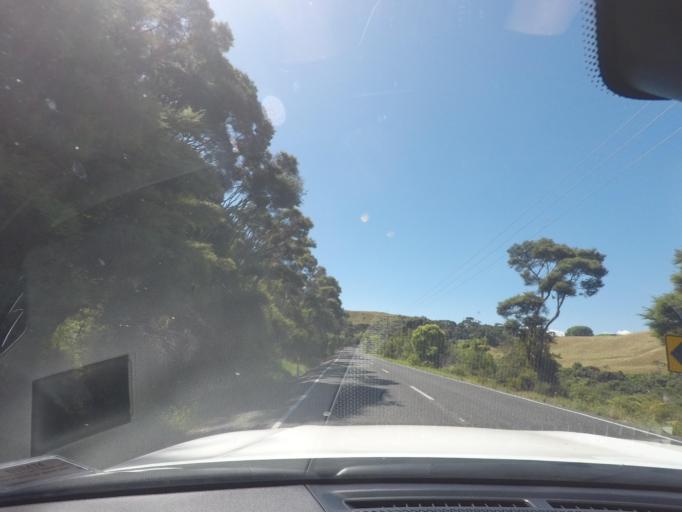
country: NZ
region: Auckland
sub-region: Auckland
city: Parakai
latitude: -36.5988
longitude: 174.3377
